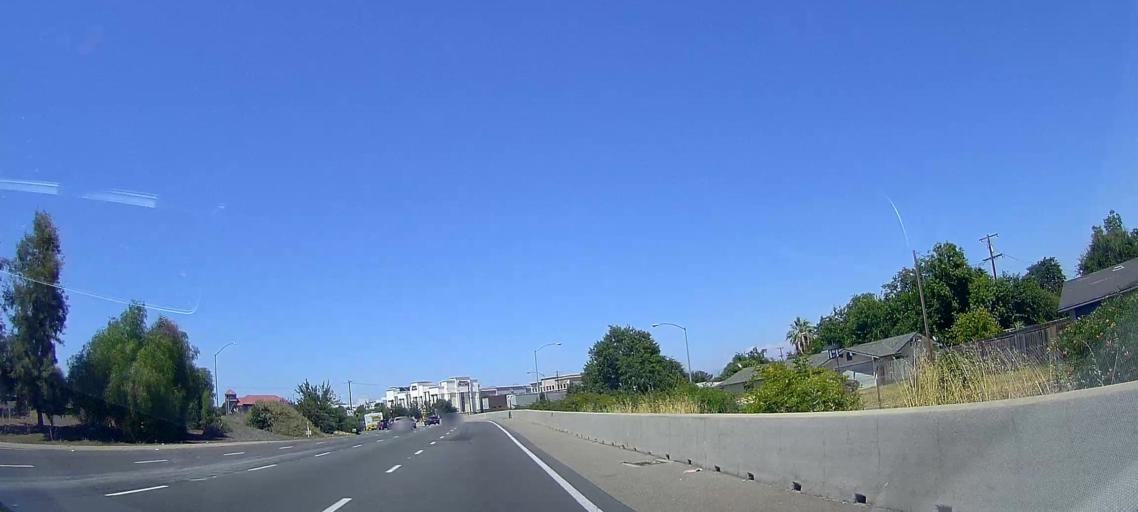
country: US
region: California
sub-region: Fresno County
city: Clovis
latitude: 36.8361
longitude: -119.7839
